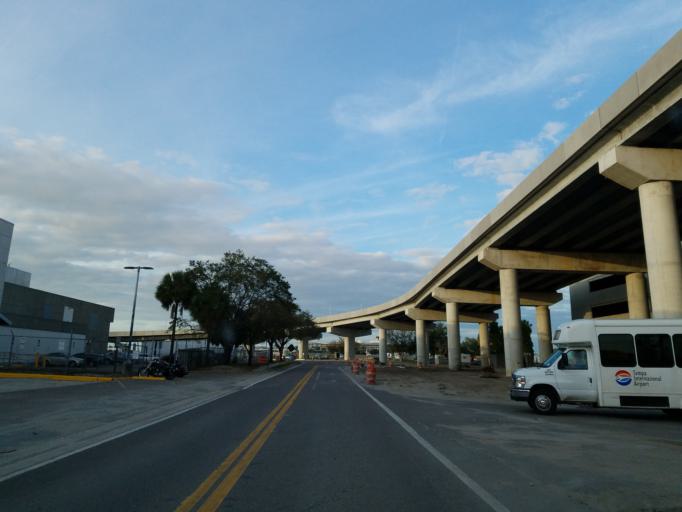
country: US
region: Florida
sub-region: Hillsborough County
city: Egypt Lake-Leto
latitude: 27.9675
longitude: -82.5359
